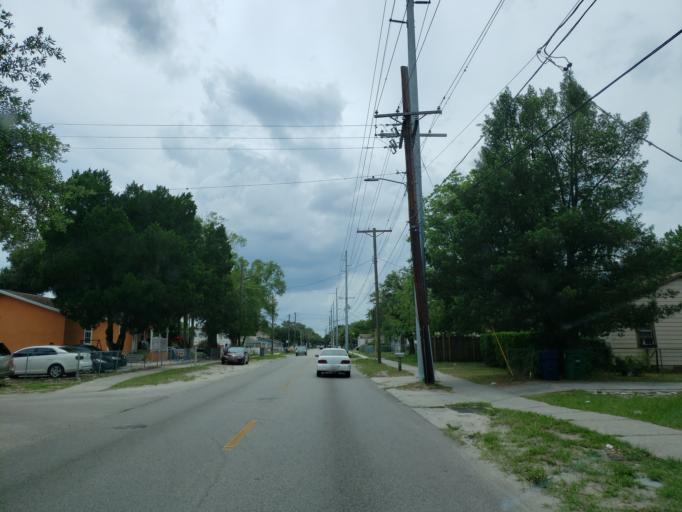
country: US
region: Florida
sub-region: Hillsborough County
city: University
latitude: 28.0253
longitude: -82.4398
